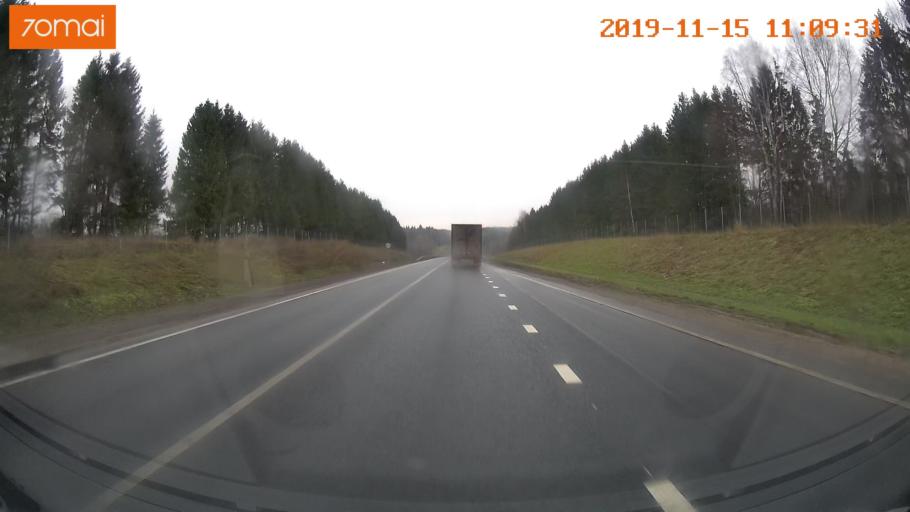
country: RU
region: Vologda
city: Chebsara
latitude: 59.1205
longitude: 39.0991
